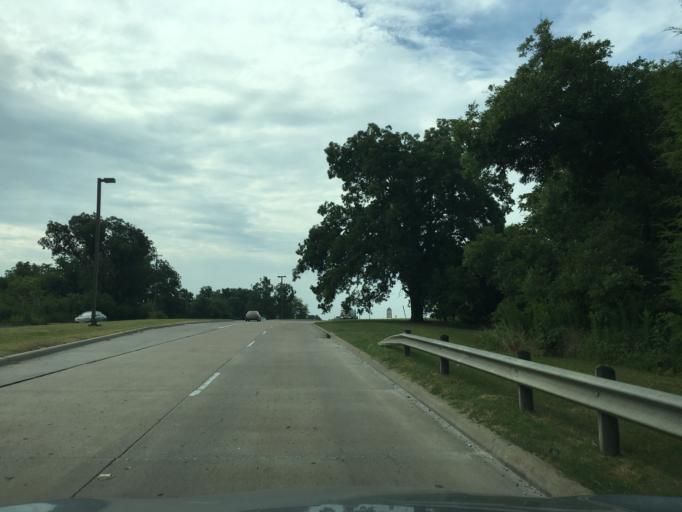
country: US
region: Texas
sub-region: Collin County
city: McKinney
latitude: 33.1957
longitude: -96.5976
